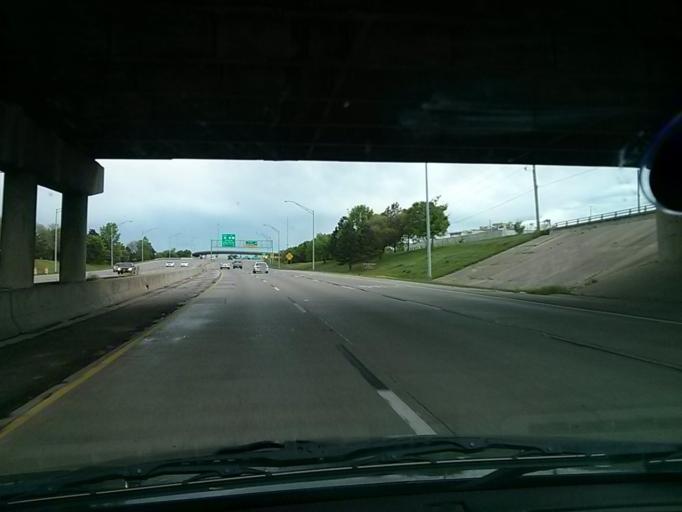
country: US
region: Oklahoma
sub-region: Tulsa County
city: Tulsa
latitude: 36.1559
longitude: -95.9806
